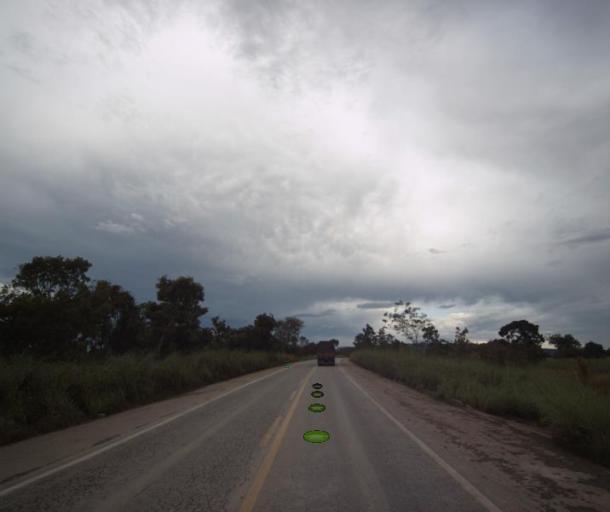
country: BR
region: Goias
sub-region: Porangatu
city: Porangatu
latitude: -13.5726
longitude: -49.0456
